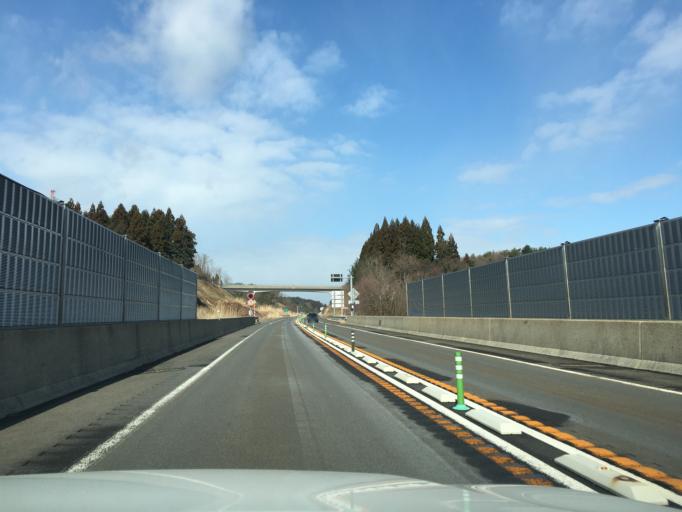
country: JP
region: Akita
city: Akita
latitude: 39.7566
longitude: 140.1363
